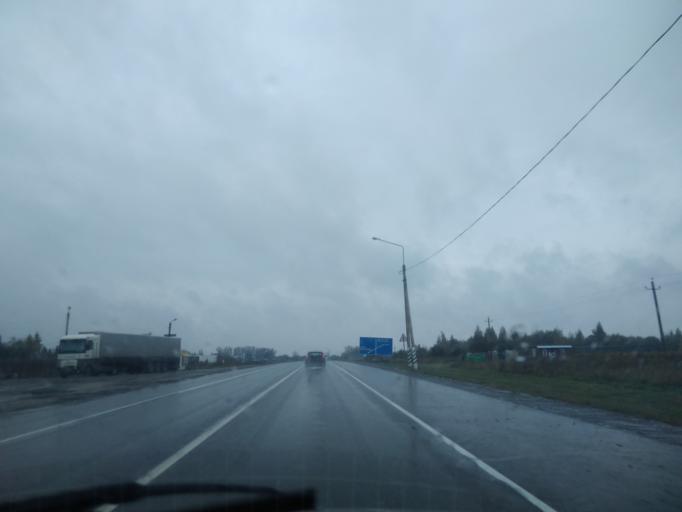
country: RU
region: Tula
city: Shchekino
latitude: 54.0017
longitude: 37.4752
